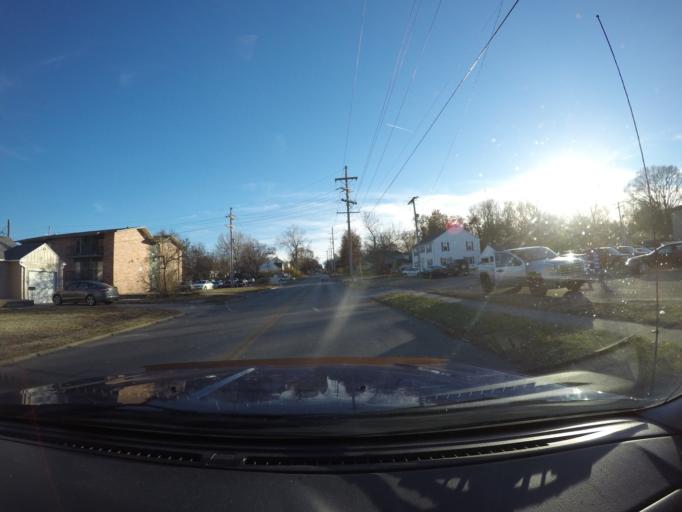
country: US
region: Kansas
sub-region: Riley County
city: Manhattan
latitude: 39.1887
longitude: -96.5888
